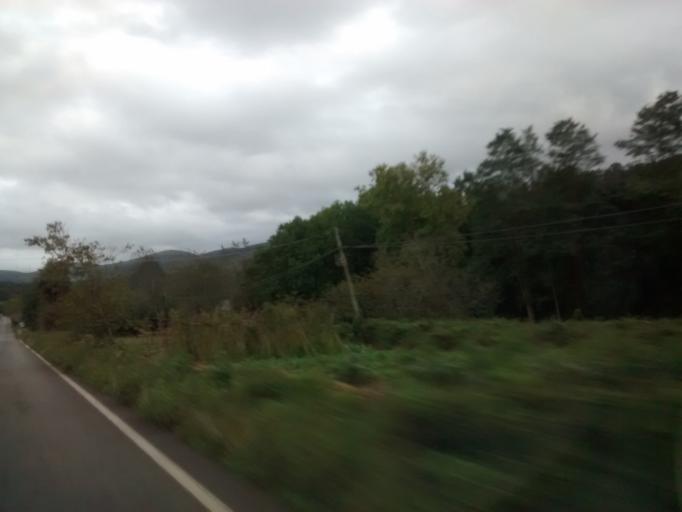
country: ES
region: Cantabria
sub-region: Provincia de Cantabria
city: Entrambasaguas
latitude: 43.3449
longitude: -3.6843
